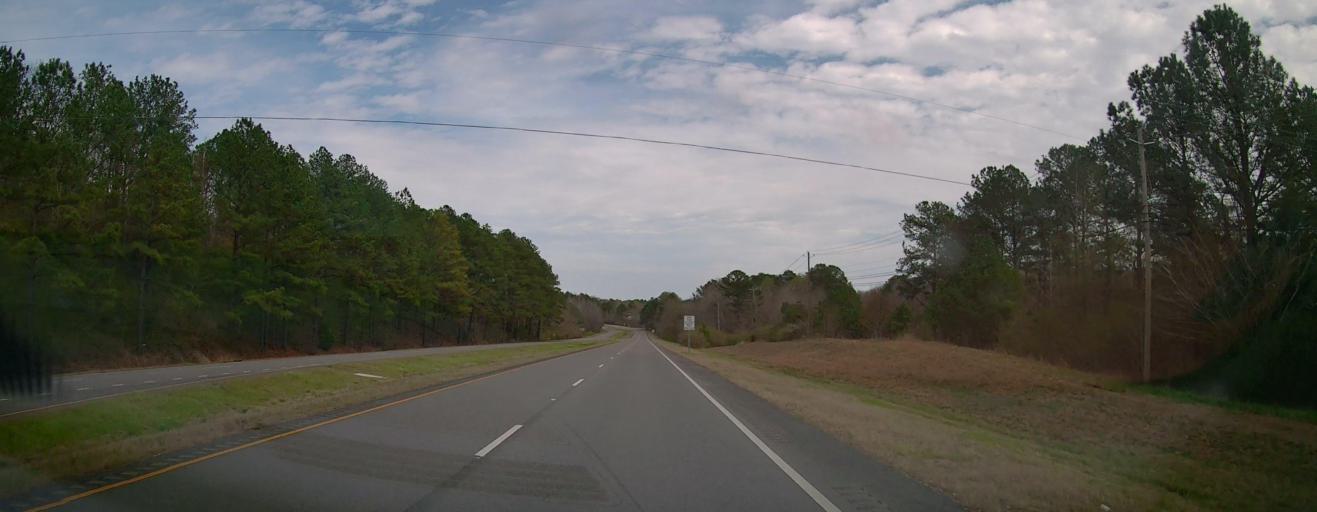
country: US
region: Alabama
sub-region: Marion County
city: Winfield
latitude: 33.9290
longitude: -87.7673
